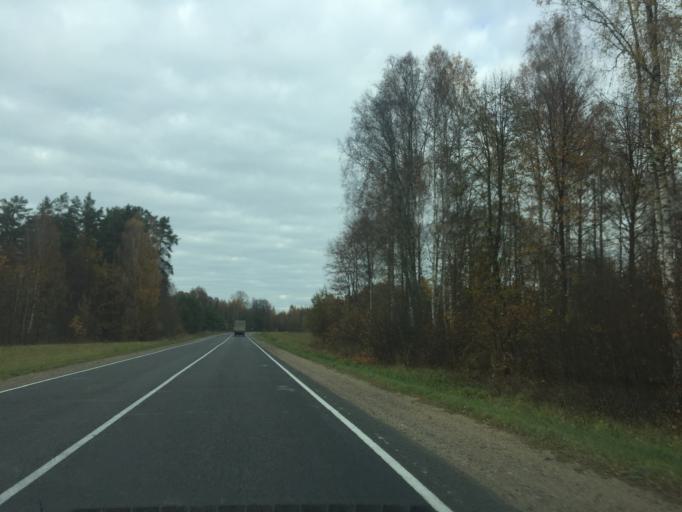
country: BY
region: Minsk
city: Svir
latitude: 54.8405
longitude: 26.1998
